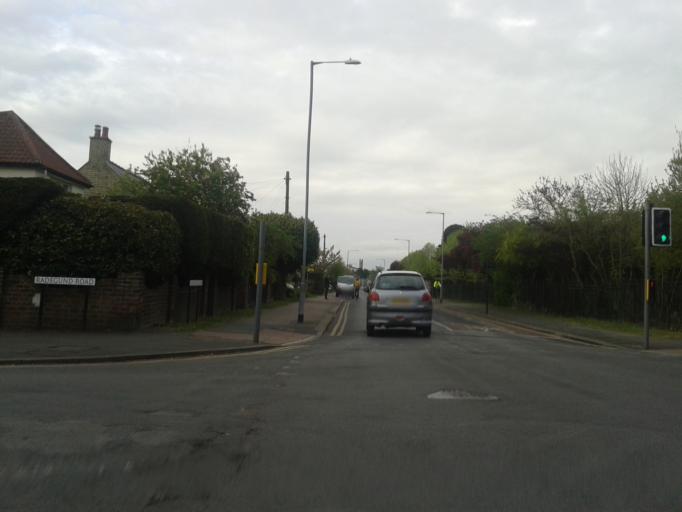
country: GB
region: England
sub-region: Cambridgeshire
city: Cambridge
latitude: 52.1930
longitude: 0.1468
